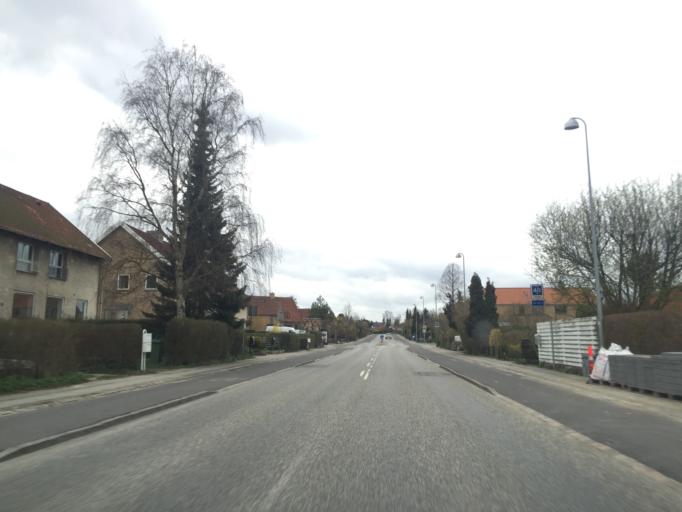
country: DK
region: Capital Region
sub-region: Rudersdal Kommune
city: Holte
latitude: 55.7946
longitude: 12.4664
